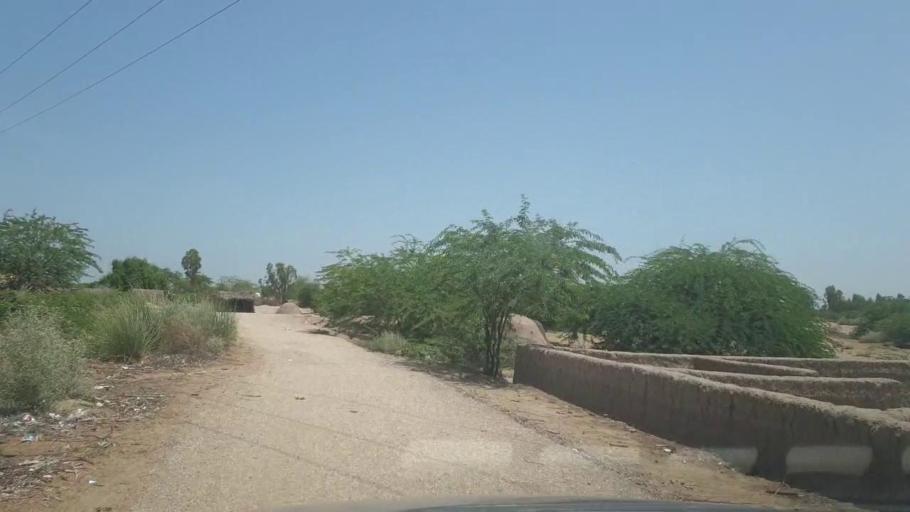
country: PK
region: Sindh
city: Kot Diji
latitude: 27.3342
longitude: 69.0098
